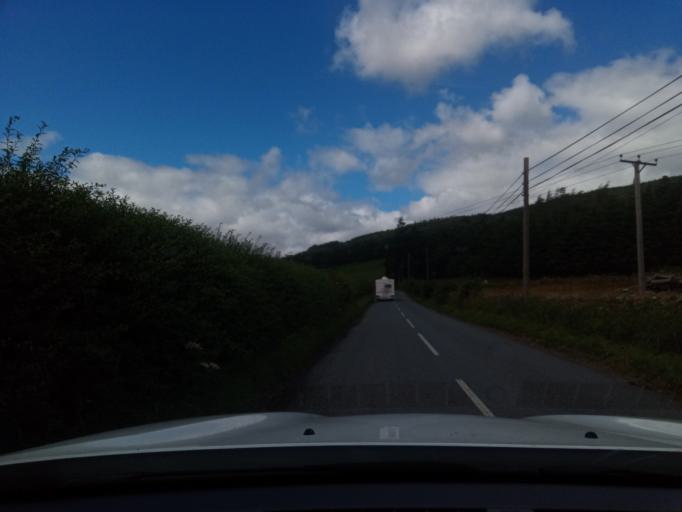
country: GB
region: Scotland
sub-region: The Scottish Borders
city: Innerleithen
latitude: 55.5558
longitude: -2.9604
